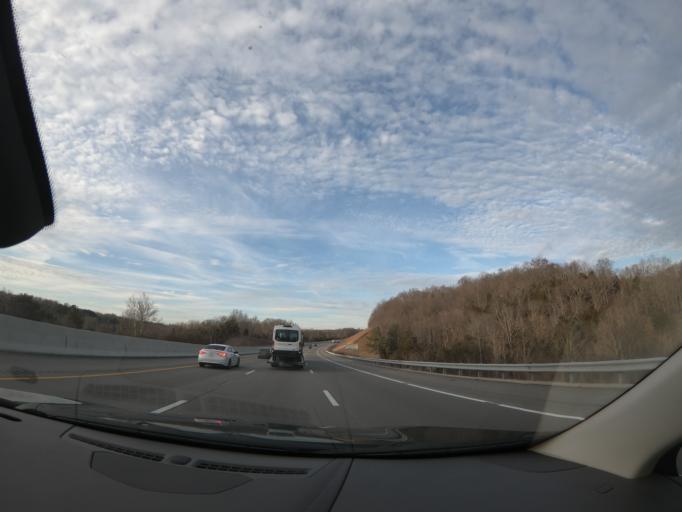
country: US
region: Kentucky
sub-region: Hart County
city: Munfordville
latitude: 37.3339
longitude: -85.9073
